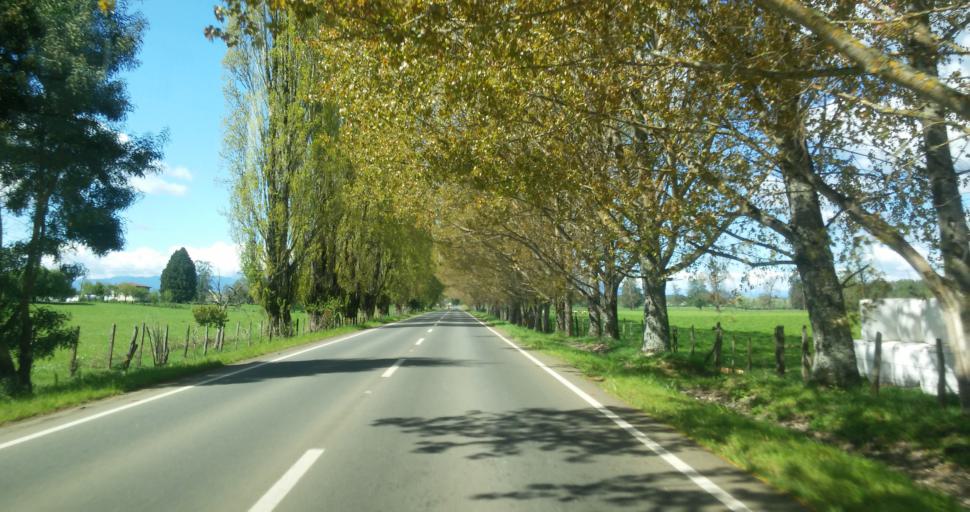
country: CL
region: Los Rios
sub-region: Provincia del Ranco
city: Rio Bueno
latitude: -40.2428
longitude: -72.6126
